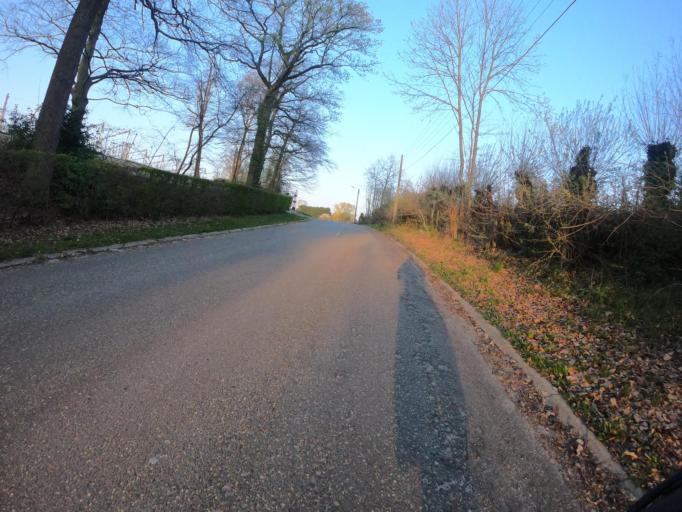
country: BE
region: Flanders
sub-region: Provincie Limburg
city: Tongeren
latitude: 50.7894
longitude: 5.4465
